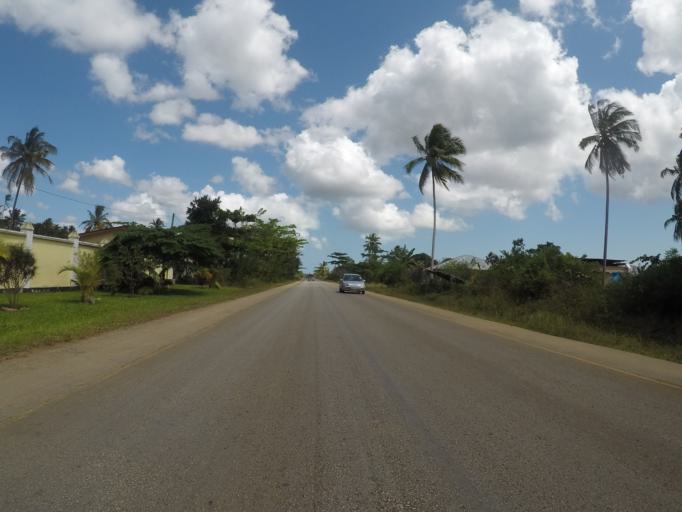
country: TZ
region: Zanzibar Central/South
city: Koani
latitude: -6.1554
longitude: 39.3296
